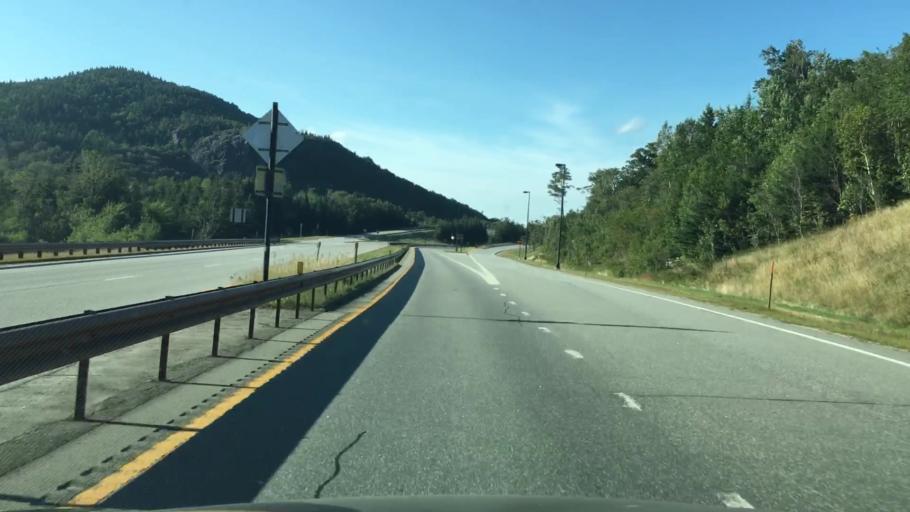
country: US
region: New Hampshire
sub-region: Grafton County
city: Deerfield
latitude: 44.1760
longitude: -71.6902
